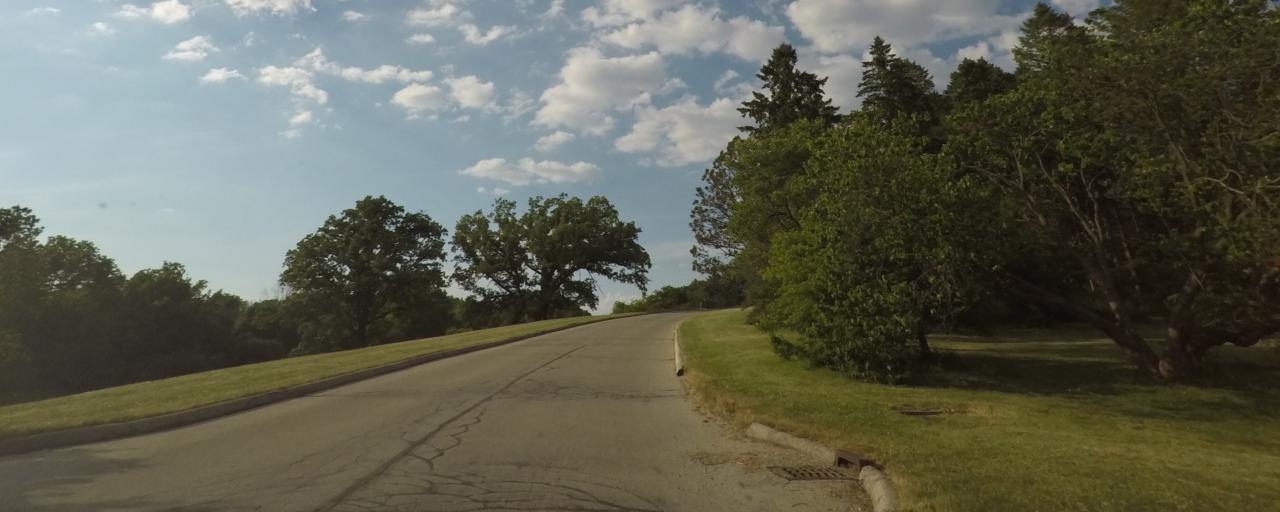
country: US
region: Wisconsin
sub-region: Milwaukee County
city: Hales Corners
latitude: 42.9322
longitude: -88.0298
